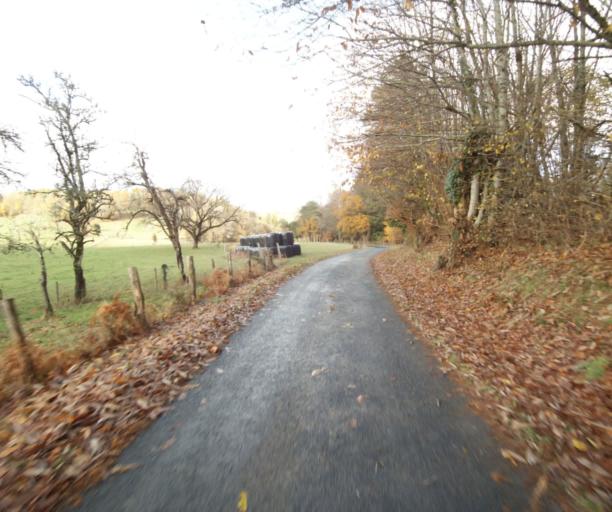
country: FR
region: Limousin
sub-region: Departement de la Correze
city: Chameyrat
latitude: 45.2262
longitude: 1.6886
